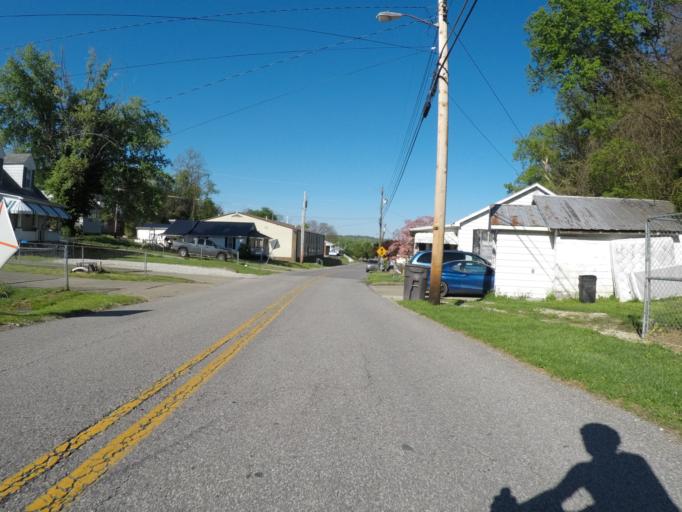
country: US
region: Kentucky
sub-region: Boyd County
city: Catlettsburg
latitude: 38.4021
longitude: -82.6032
